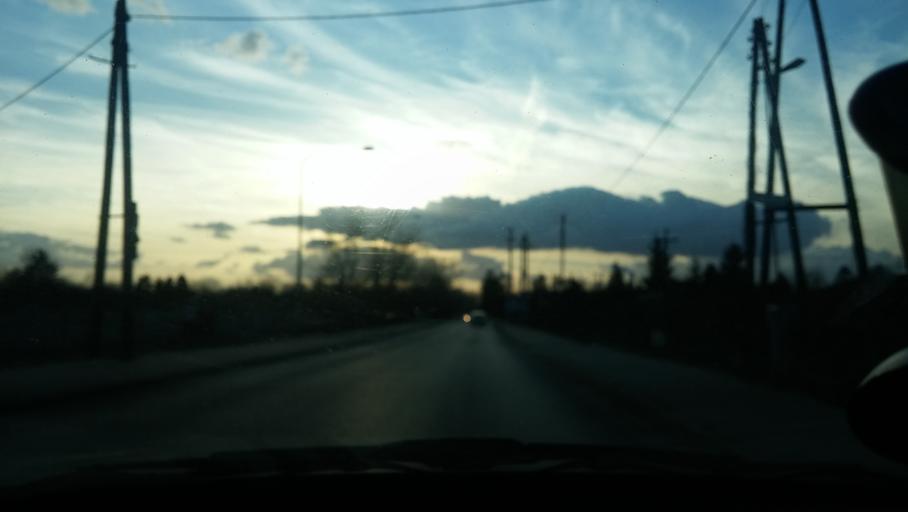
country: PL
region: Masovian Voivodeship
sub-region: Warszawa
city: Wawer
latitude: 52.1846
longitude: 21.1405
